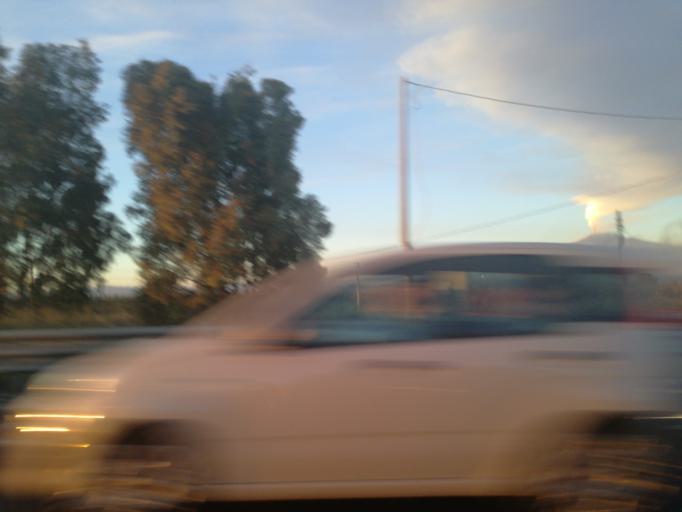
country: IT
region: Sicily
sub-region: Catania
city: Motta Sant'Anastasia
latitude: 37.4293
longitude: 14.9363
